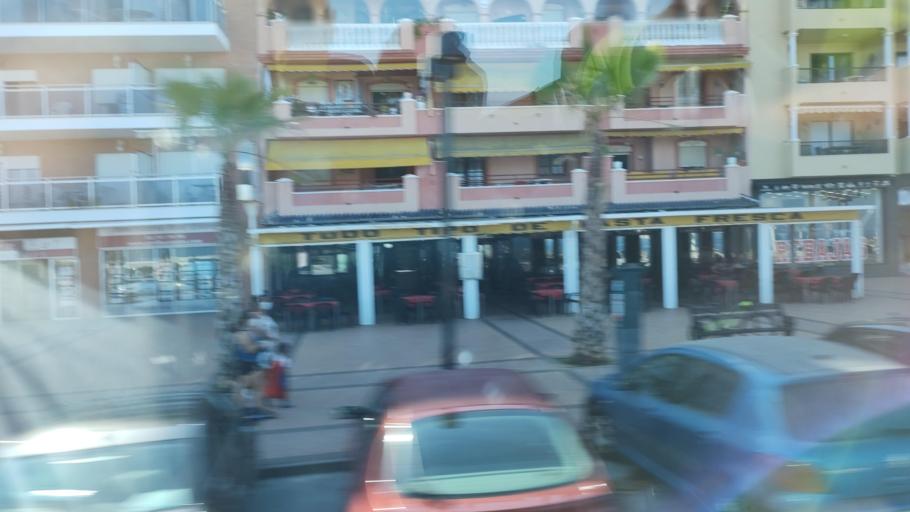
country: ES
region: Andalusia
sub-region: Provincia de Malaga
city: Fuengirola
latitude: 36.5448
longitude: -4.6179
